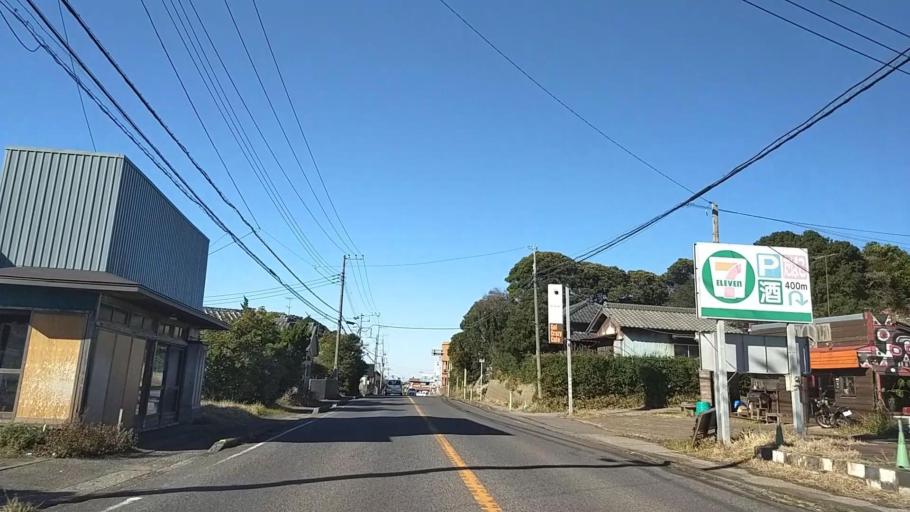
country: JP
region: Chiba
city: Ohara
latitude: 35.3283
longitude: 140.3976
